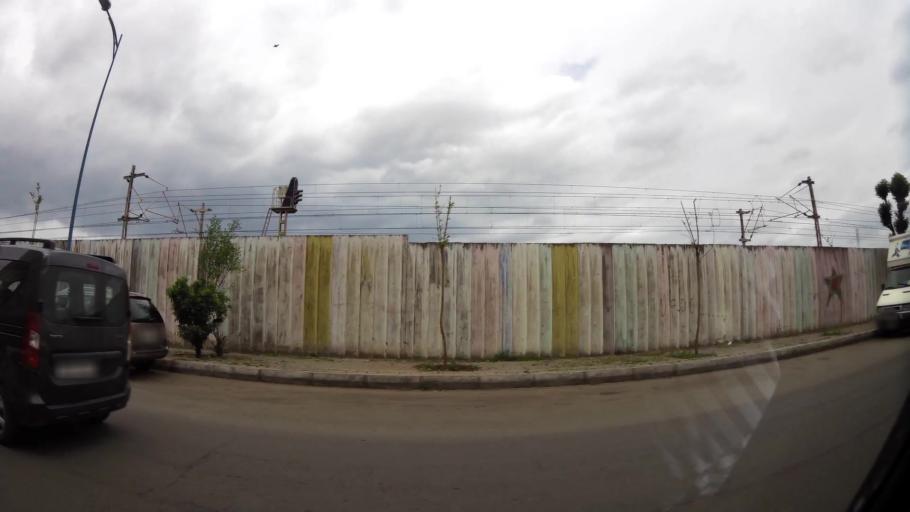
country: MA
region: Grand Casablanca
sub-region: Casablanca
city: Casablanca
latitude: 33.5958
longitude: -7.5594
